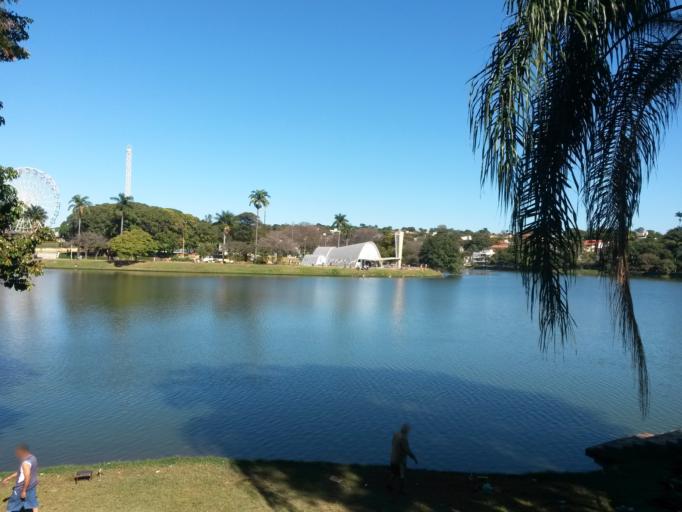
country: BR
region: Minas Gerais
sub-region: Belo Horizonte
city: Belo Horizonte
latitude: -19.8577
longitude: -43.9770
